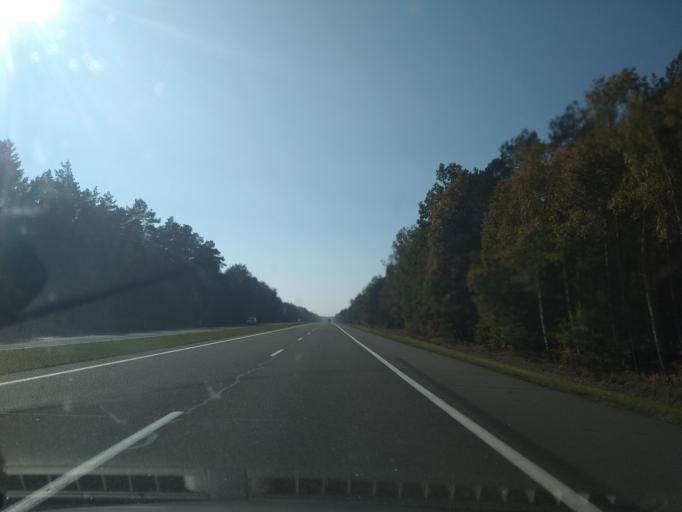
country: BY
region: Brest
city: Antopal'
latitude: 52.3817
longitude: 24.7617
